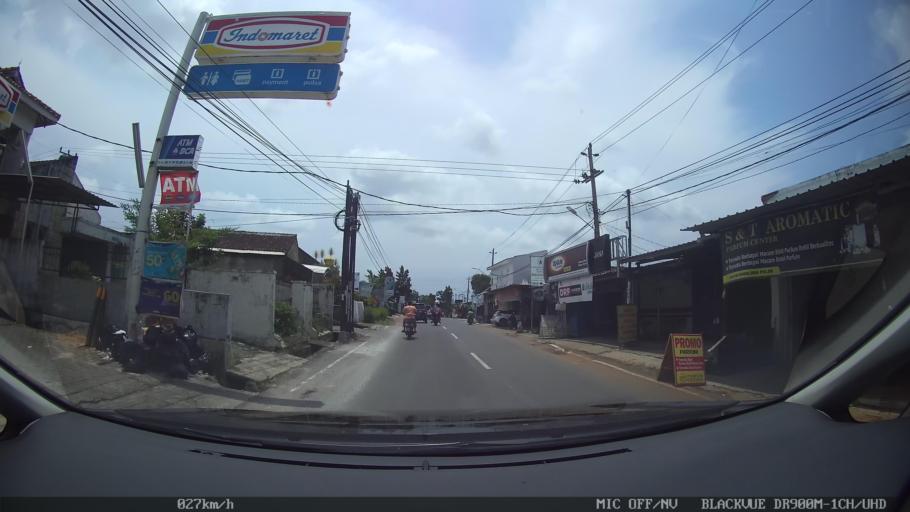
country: ID
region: Lampung
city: Kedaton
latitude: -5.3885
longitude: 105.2493
